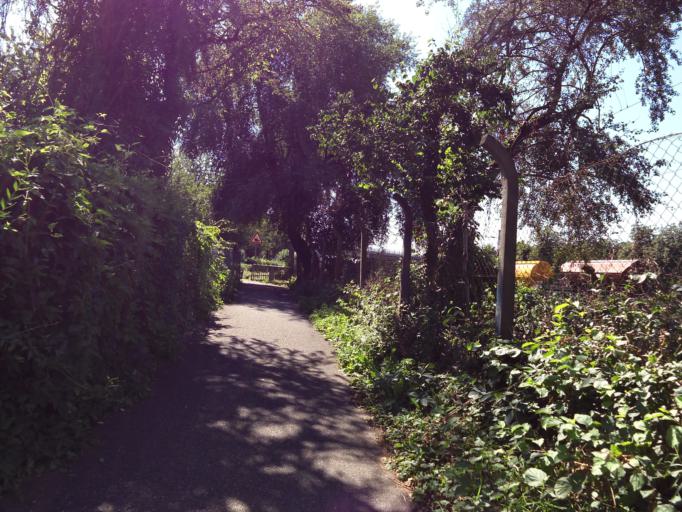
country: DE
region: Hesse
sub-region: Regierungsbezirk Darmstadt
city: Ginsheim-Gustavsburg
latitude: 49.9733
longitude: 8.3145
